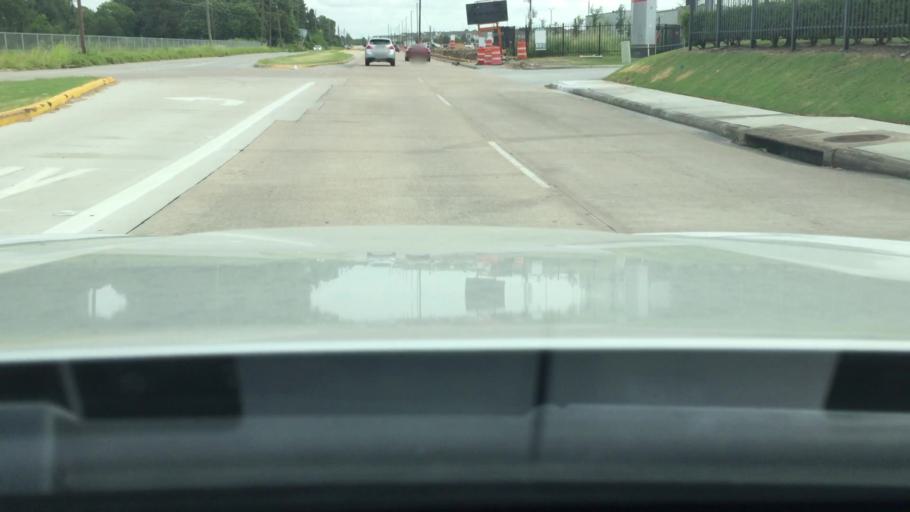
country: US
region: Texas
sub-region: Harris County
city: Jersey Village
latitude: 29.9414
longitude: -95.5467
